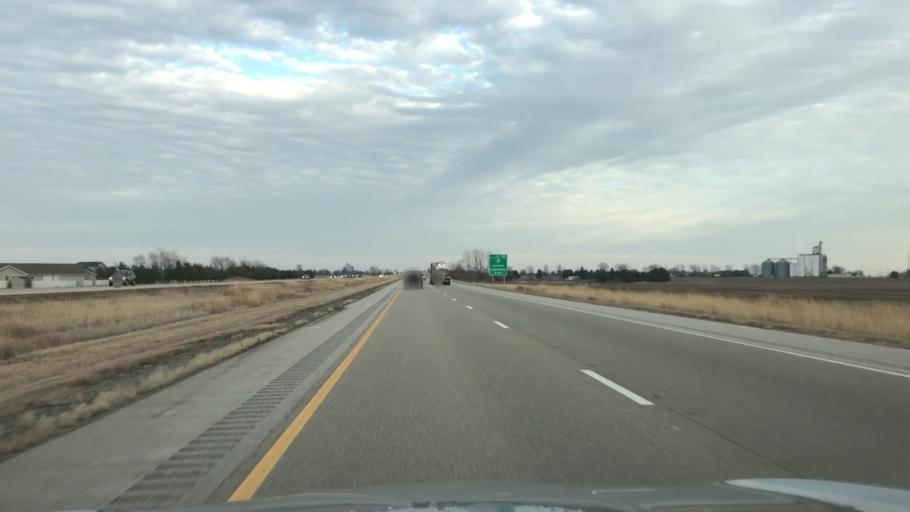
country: US
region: Illinois
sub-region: Logan County
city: Lincoln
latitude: 40.1832
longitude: -89.3416
